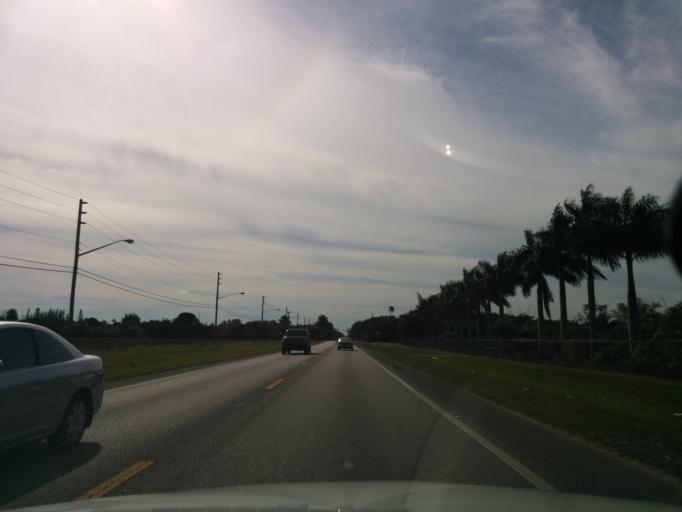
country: US
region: Florida
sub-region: Miami-Dade County
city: Homestead
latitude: 25.4950
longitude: -80.4776
